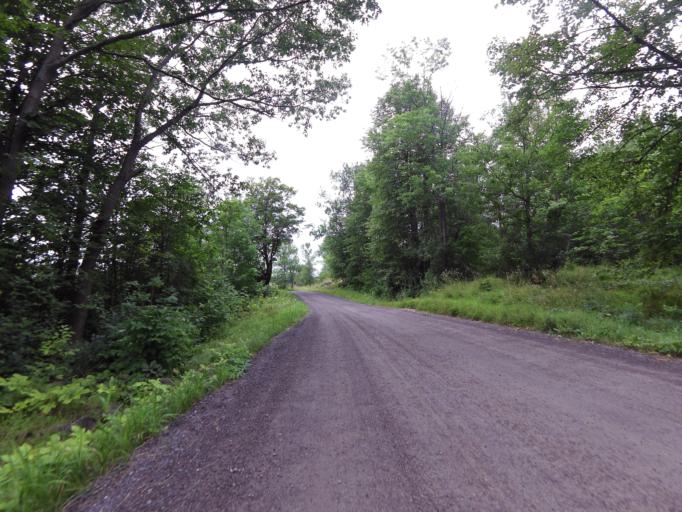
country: CA
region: Ontario
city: Perth
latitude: 44.6826
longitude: -76.6458
